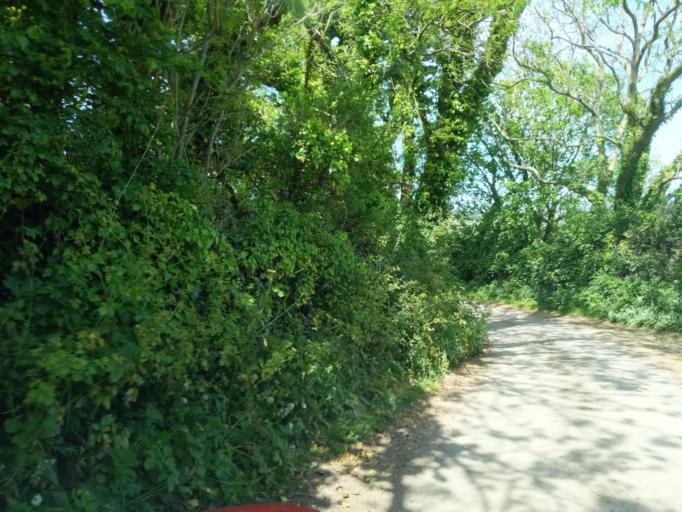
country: GB
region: England
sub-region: Borough of Torbay
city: Brixham
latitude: 50.3646
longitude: -3.5301
